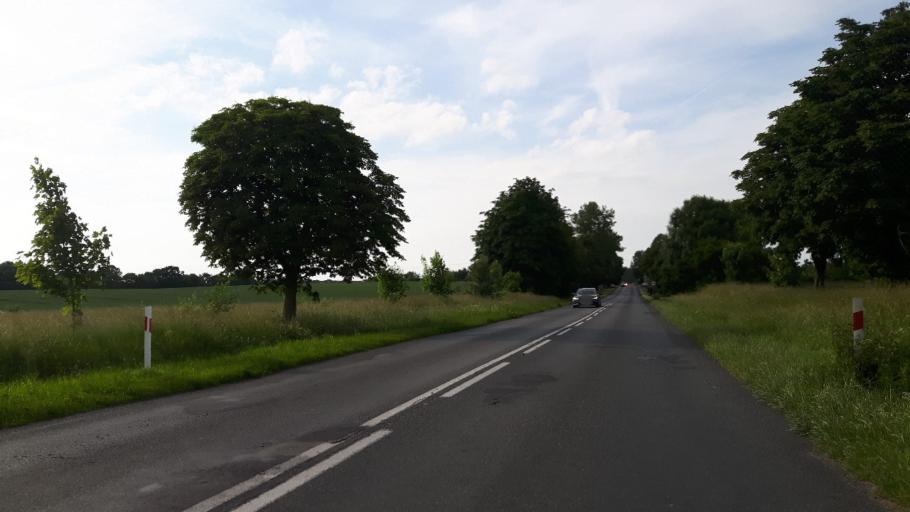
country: PL
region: West Pomeranian Voivodeship
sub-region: Powiat gryficki
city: Gryfice
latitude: 53.8995
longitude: 15.2041
